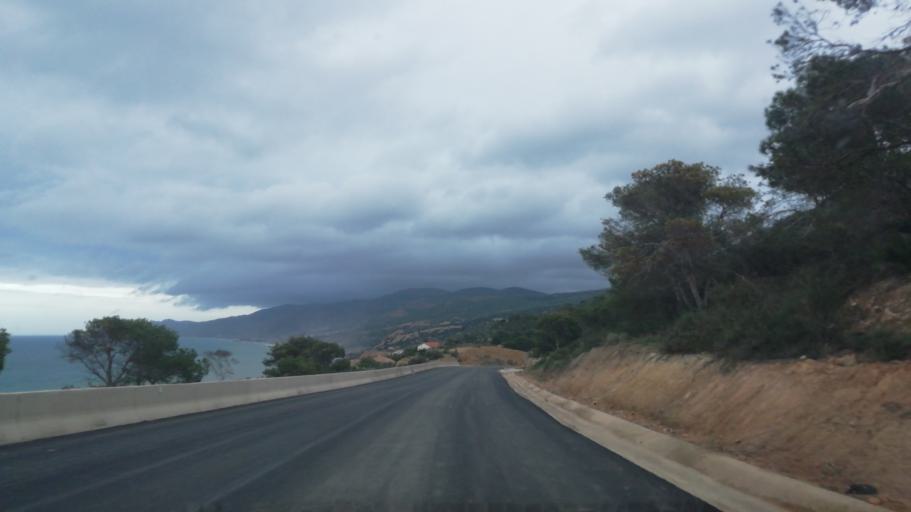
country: DZ
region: Oran
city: Bir el Djir
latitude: 35.7780
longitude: -0.5132
